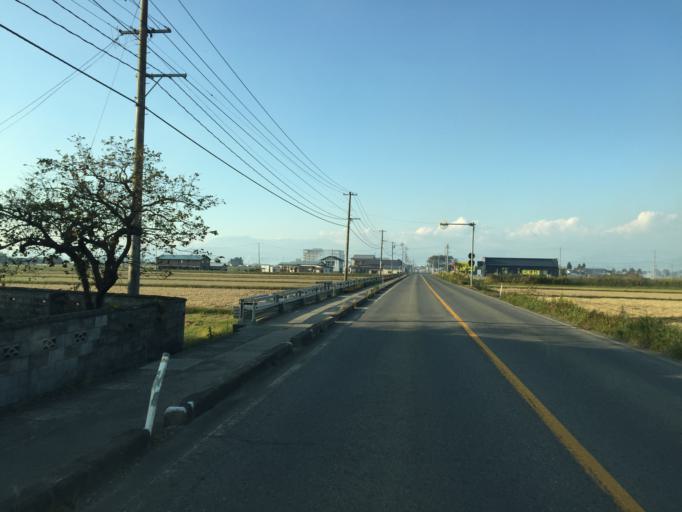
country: JP
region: Fukushima
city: Kitakata
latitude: 37.5449
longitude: 139.9123
